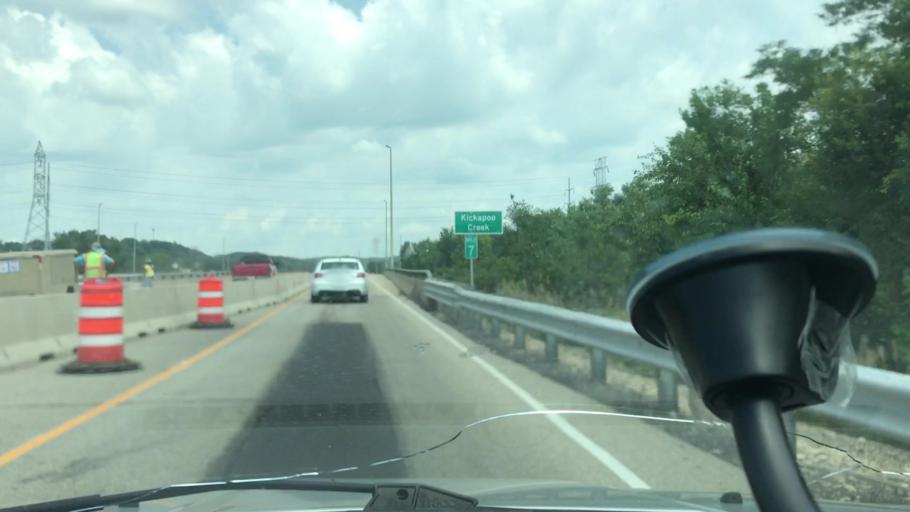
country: US
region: Illinois
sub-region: Peoria County
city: Bartonville
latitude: 40.6533
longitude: -89.6399
